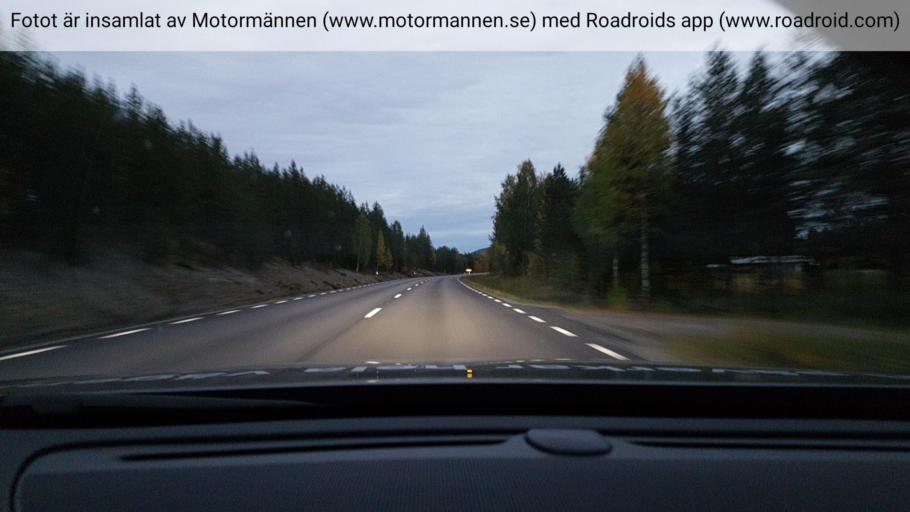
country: SE
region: Norrbotten
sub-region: Alvsbyns Kommun
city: AElvsbyn
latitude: 65.7368
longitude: 20.9720
